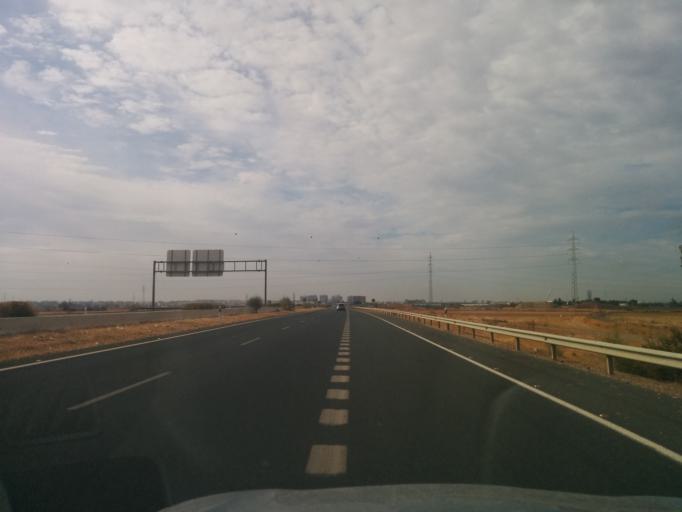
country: ES
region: Andalusia
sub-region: Provincia de Sevilla
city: La Rinconada
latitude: 37.4510
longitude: -5.9708
